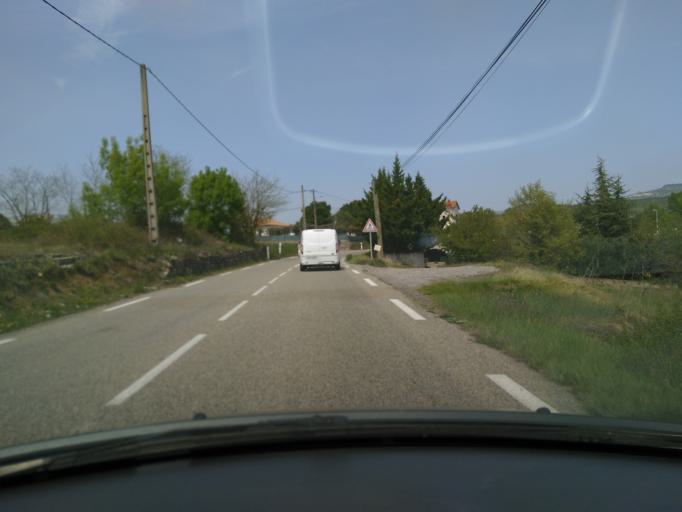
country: FR
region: Rhone-Alpes
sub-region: Departement de l'Ardeche
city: Lavilledieu
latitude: 44.5660
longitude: 4.4607
